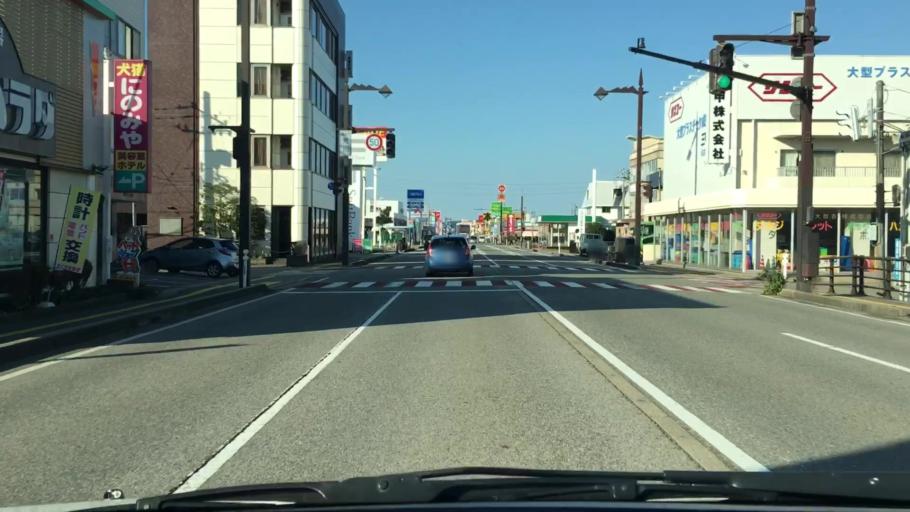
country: JP
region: Toyama
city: Toyama-shi
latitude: 36.6963
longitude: 137.2493
